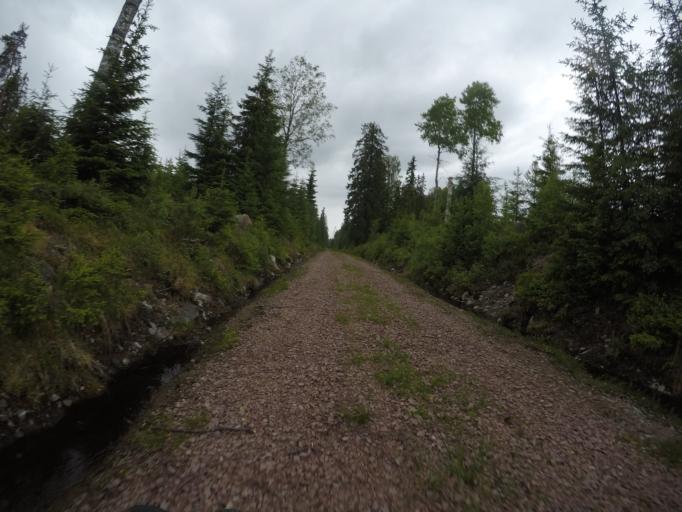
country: SE
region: OErebro
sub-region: Hallefors Kommun
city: Haellefors
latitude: 60.0220
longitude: 14.5784
